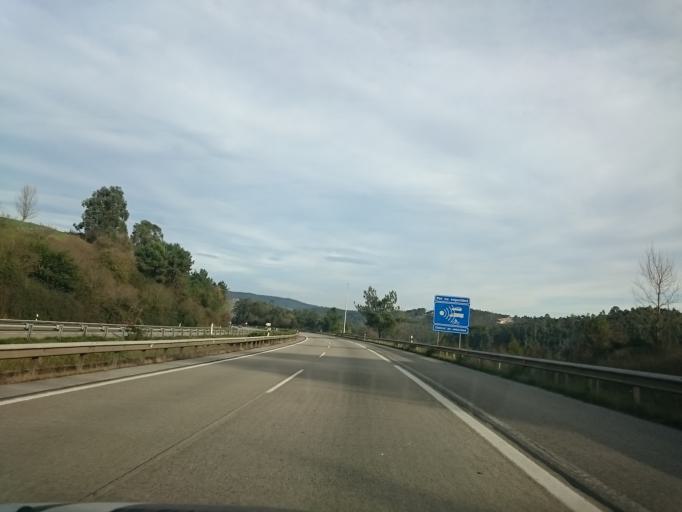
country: ES
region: Asturias
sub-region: Province of Asturias
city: Lugones
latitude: 43.4694
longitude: -5.7901
